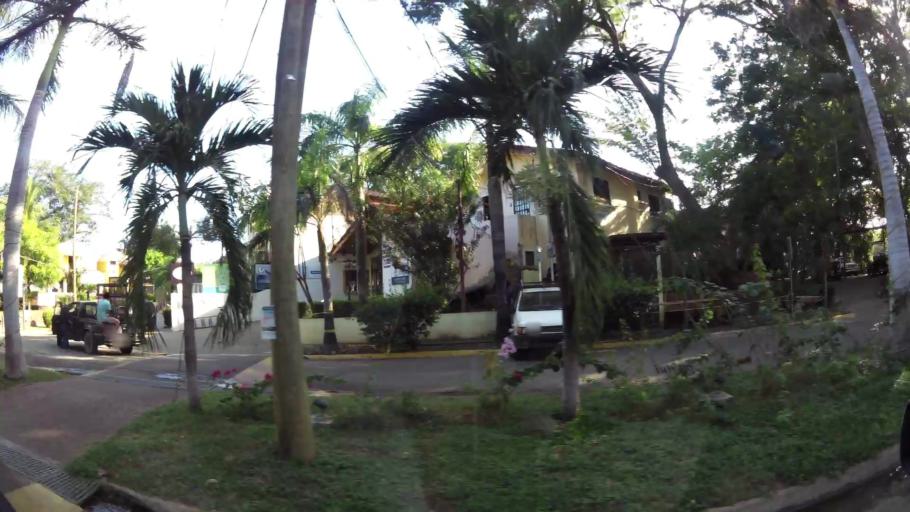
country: CR
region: Guanacaste
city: Sardinal
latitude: 10.5543
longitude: -85.6924
